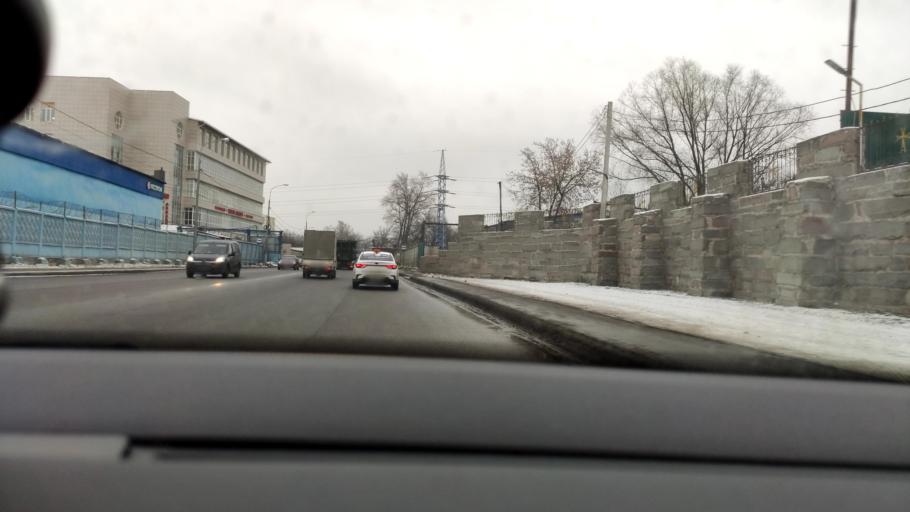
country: RU
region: Moscow
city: Khimki
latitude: 55.9065
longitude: 37.4254
